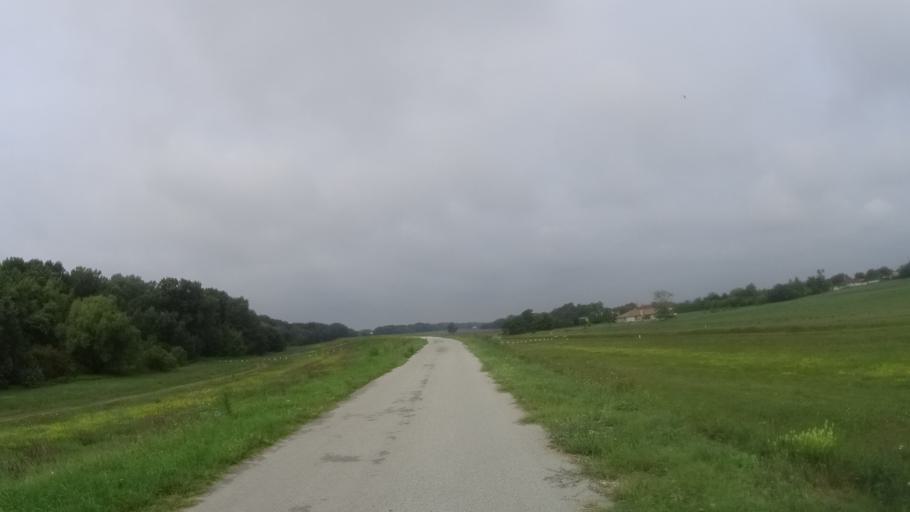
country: SK
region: Nitriansky
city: Komarno
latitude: 47.7438
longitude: 18.1829
